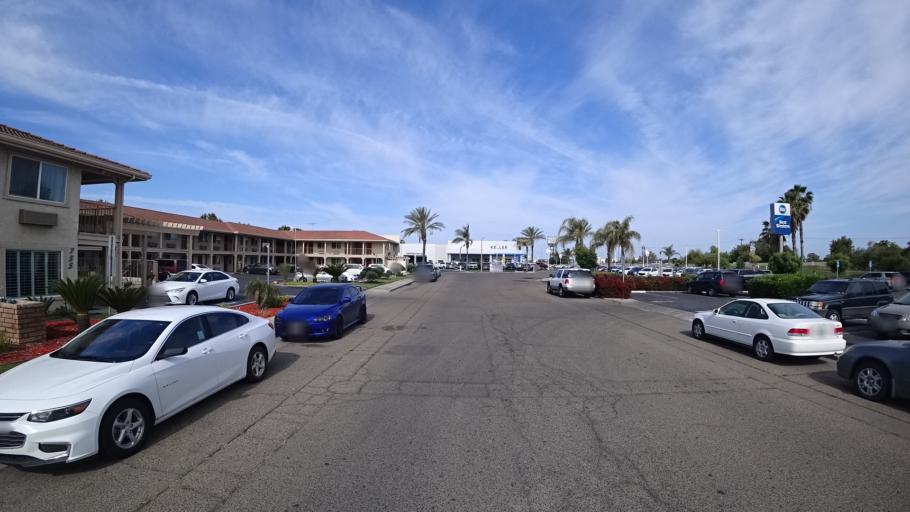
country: US
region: California
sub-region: Kings County
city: Hanford
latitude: 36.3203
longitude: -119.6562
